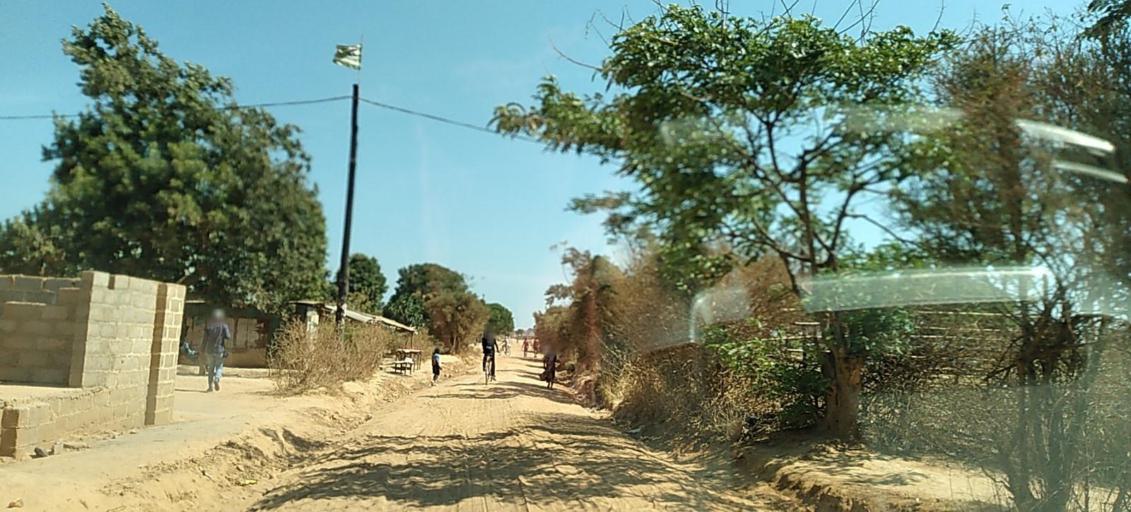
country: ZM
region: Copperbelt
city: Chililabombwe
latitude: -12.3315
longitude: 27.8602
